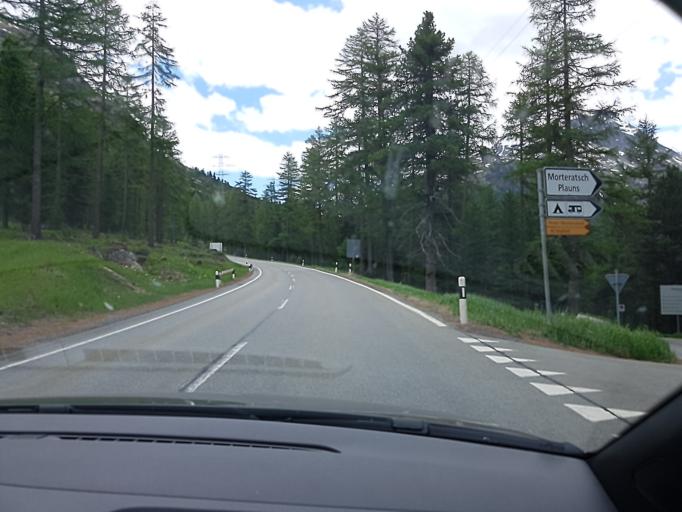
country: CH
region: Grisons
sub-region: Maloja District
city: Pontresina
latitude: 46.4629
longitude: 9.9354
